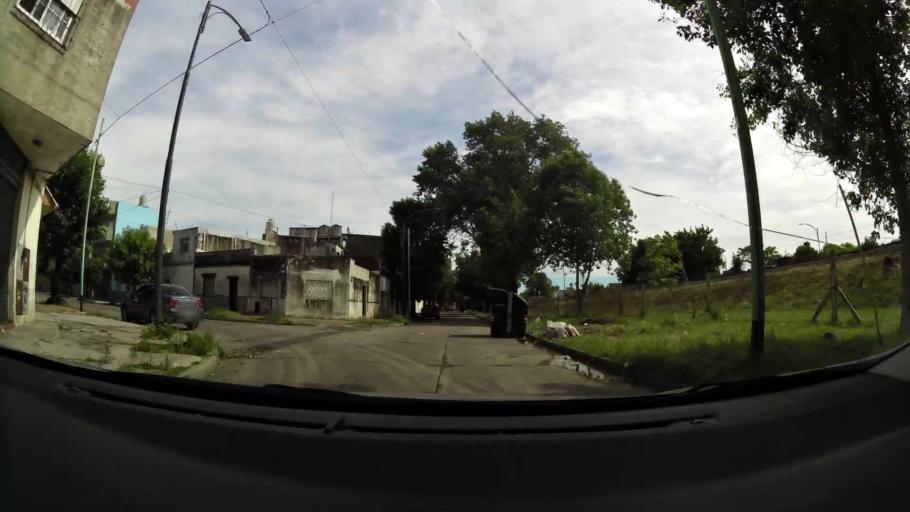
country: AR
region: Buenos Aires F.D.
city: Villa Lugano
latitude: -34.6563
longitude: -58.4313
